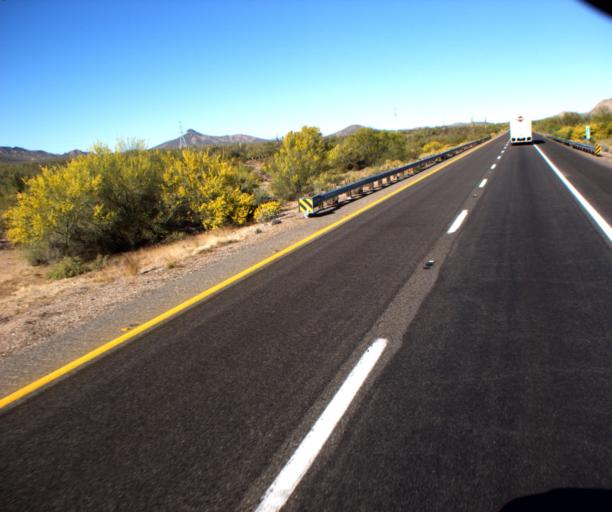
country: US
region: Arizona
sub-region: Pinal County
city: Maricopa
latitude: 32.8333
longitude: -112.0929
